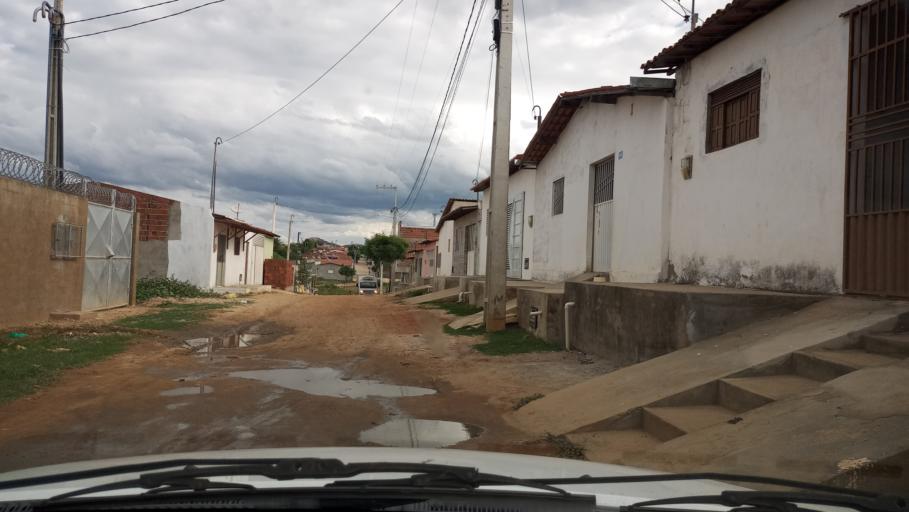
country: BR
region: Rio Grande do Norte
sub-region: Sao Tome
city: Sao Tome
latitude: -5.9429
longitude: -35.9261
